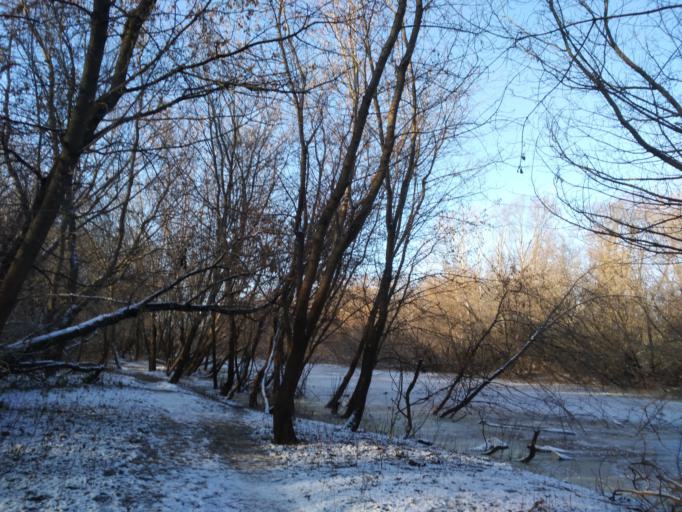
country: RU
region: Kirov
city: Vyatskiye Polyany
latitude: 56.2380
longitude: 51.0797
